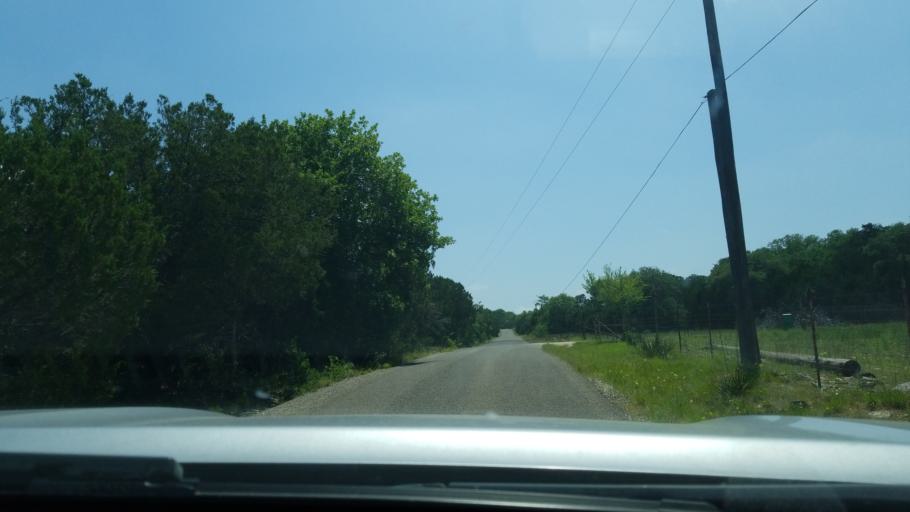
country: US
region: Texas
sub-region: Blanco County
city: Blanco
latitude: 30.0849
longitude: -98.3999
